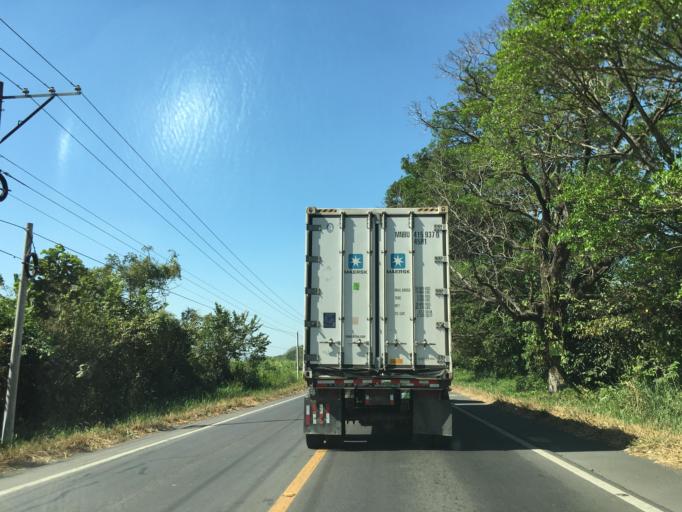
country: GT
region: Escuintla
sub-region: Municipio de Masagua
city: Masagua
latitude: 14.1897
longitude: -90.8576
